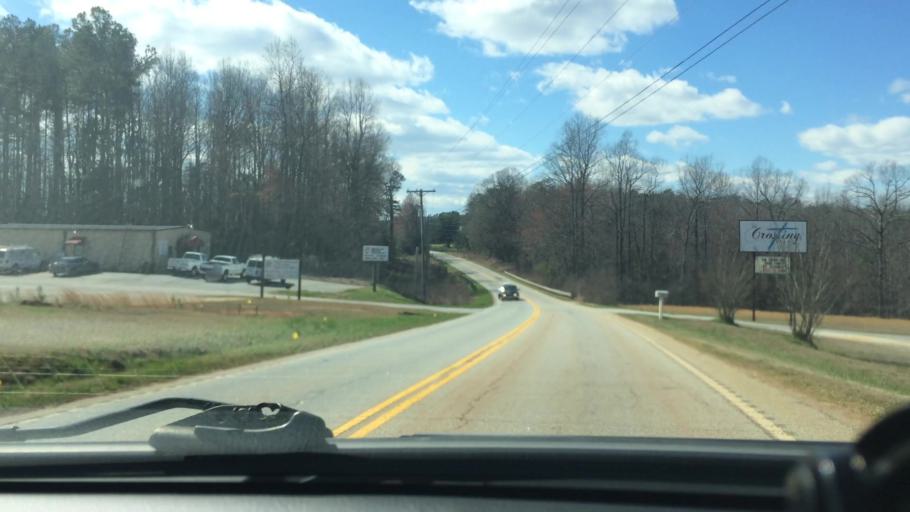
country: US
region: South Carolina
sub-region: Pickens County
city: Easley
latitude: 34.8912
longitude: -82.5811
